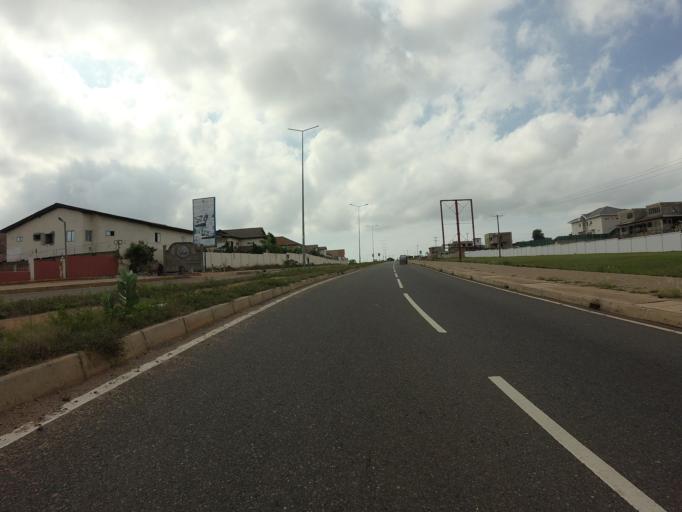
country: GH
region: Greater Accra
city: Teshi Old Town
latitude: 5.6091
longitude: -0.1408
